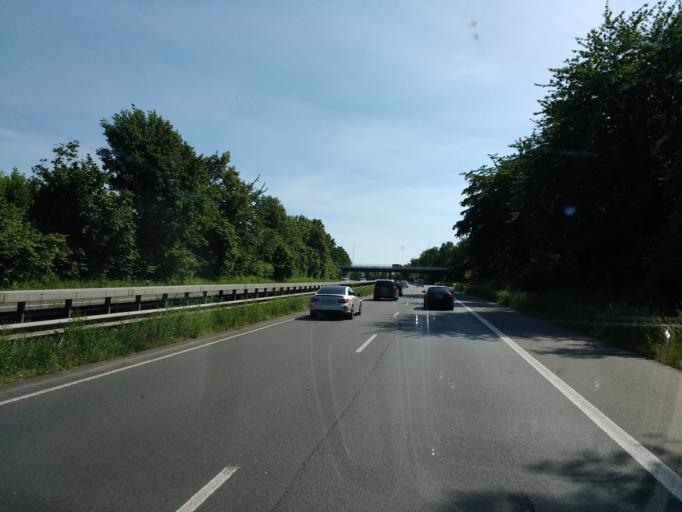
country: DE
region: North Rhine-Westphalia
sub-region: Regierungsbezirk Detmold
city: Herford
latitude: 52.1246
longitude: 8.6431
